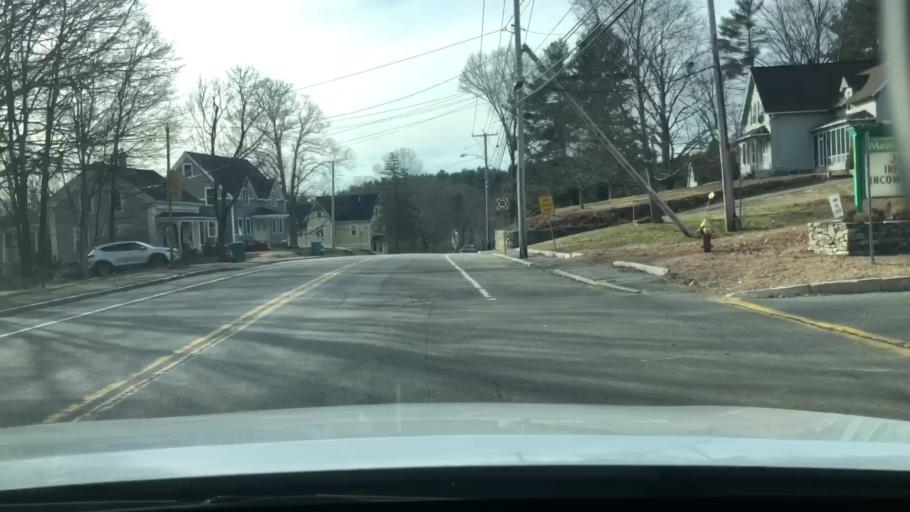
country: US
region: Massachusetts
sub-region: Worcester County
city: Upton
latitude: 42.1692
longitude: -71.6122
